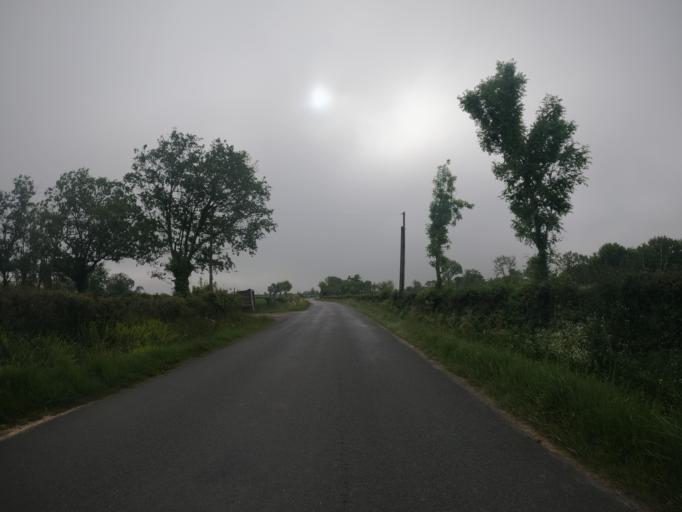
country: FR
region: Poitou-Charentes
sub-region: Departement des Deux-Sevres
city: Chiche
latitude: 46.8758
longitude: -0.3209
